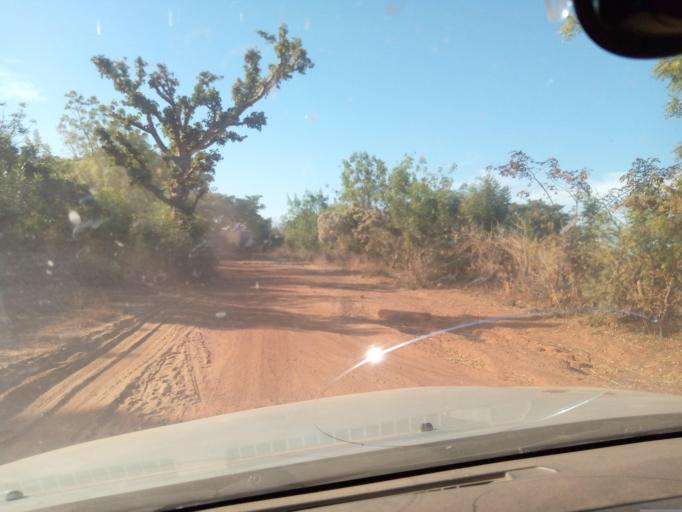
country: ML
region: Sikasso
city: Sikasso
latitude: 11.4791
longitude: -5.4773
